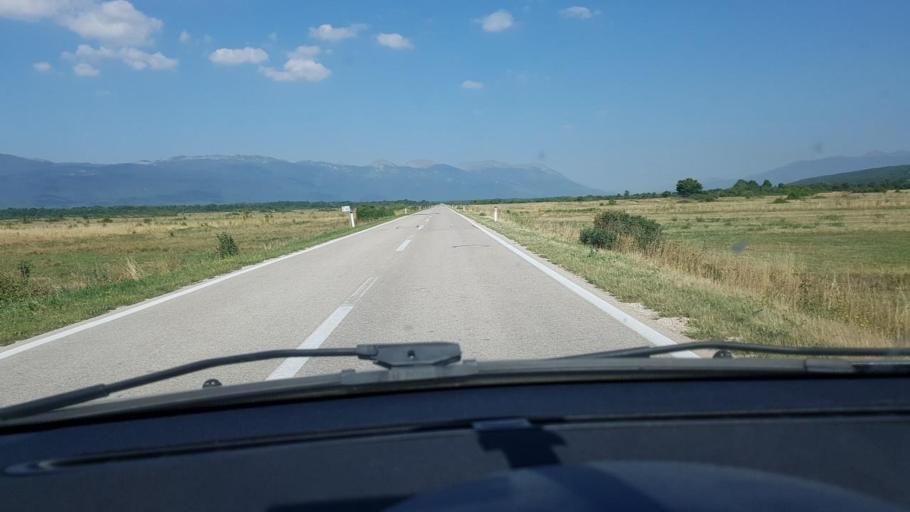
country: BA
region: Federation of Bosnia and Herzegovina
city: Glamoc
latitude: 43.9665
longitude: 16.7345
